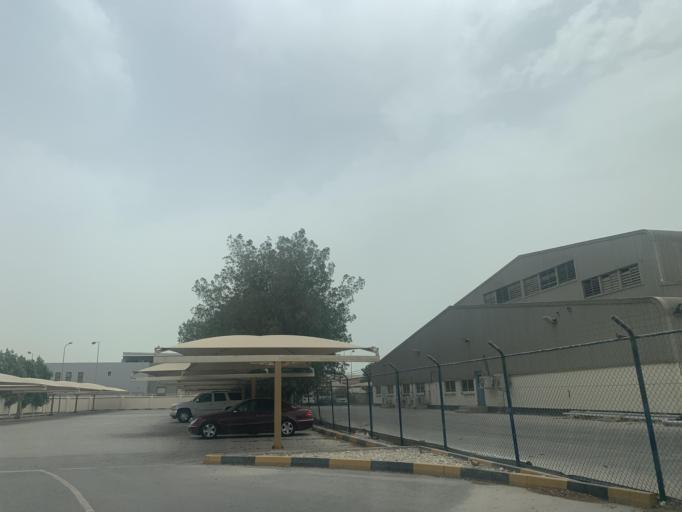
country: BH
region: Northern
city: Sitrah
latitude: 26.1791
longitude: 50.6144
